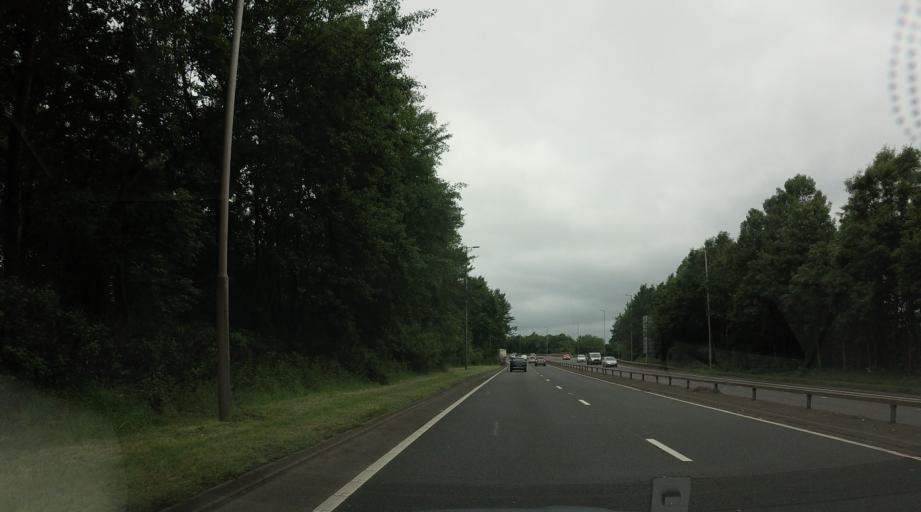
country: GB
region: Scotland
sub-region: South Lanarkshire
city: Bothwell
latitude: 55.7918
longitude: -4.0741
